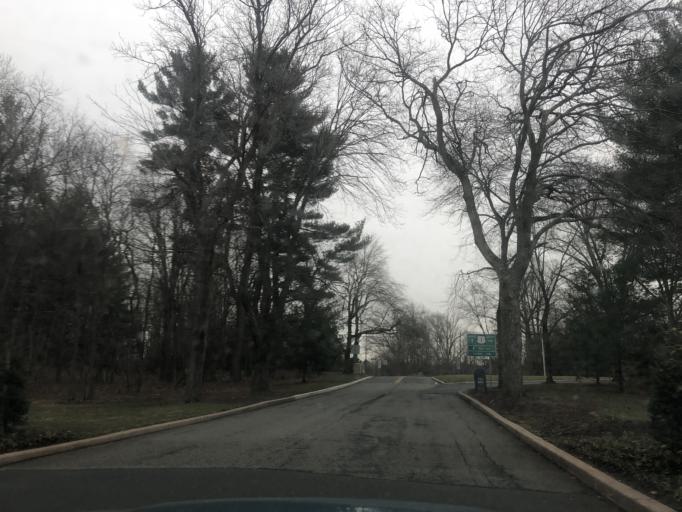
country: US
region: New Jersey
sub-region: Somerset County
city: Kingston
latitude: 40.3499
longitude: -74.6193
